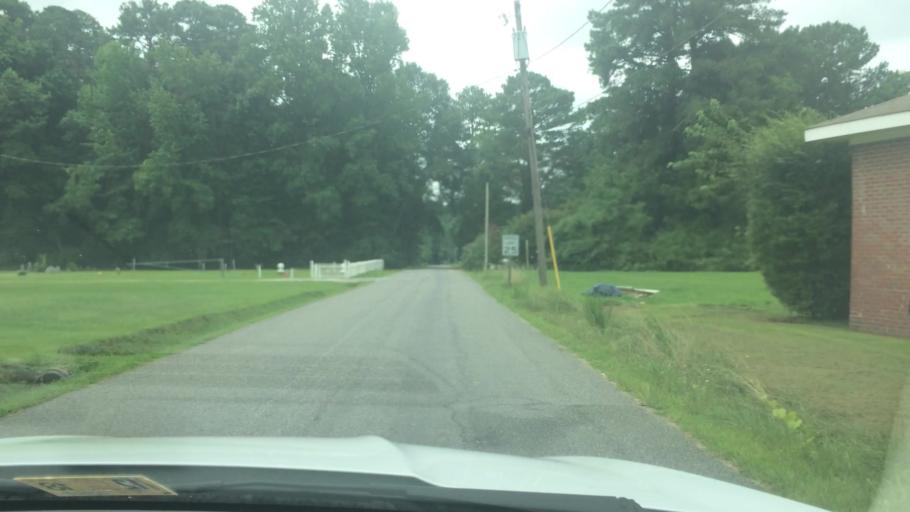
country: US
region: Virginia
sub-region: York County
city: Yorktown
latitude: 37.2325
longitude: -76.5460
